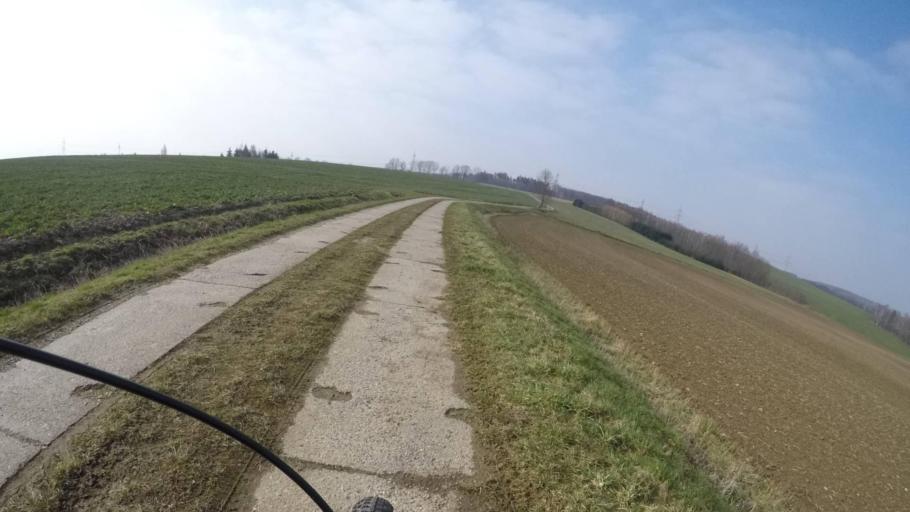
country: DE
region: Saxony
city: Callenberg
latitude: 50.8864
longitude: 12.6509
